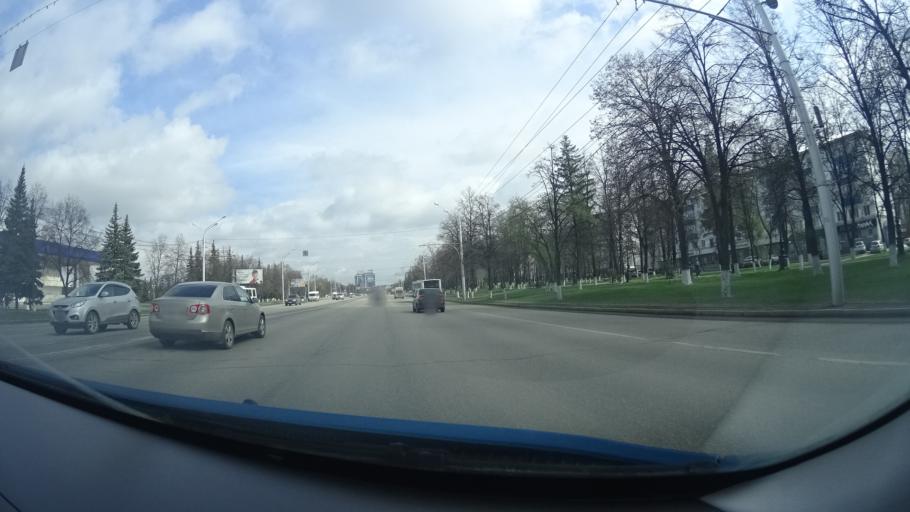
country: RU
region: Bashkortostan
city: Ufa
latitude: 54.7704
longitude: 56.0236
